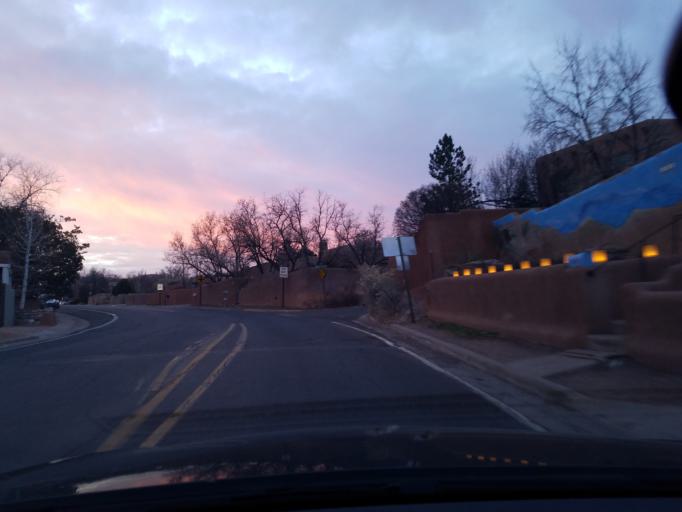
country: US
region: New Mexico
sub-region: Santa Fe County
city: Santa Fe
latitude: 35.6932
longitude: -105.9342
